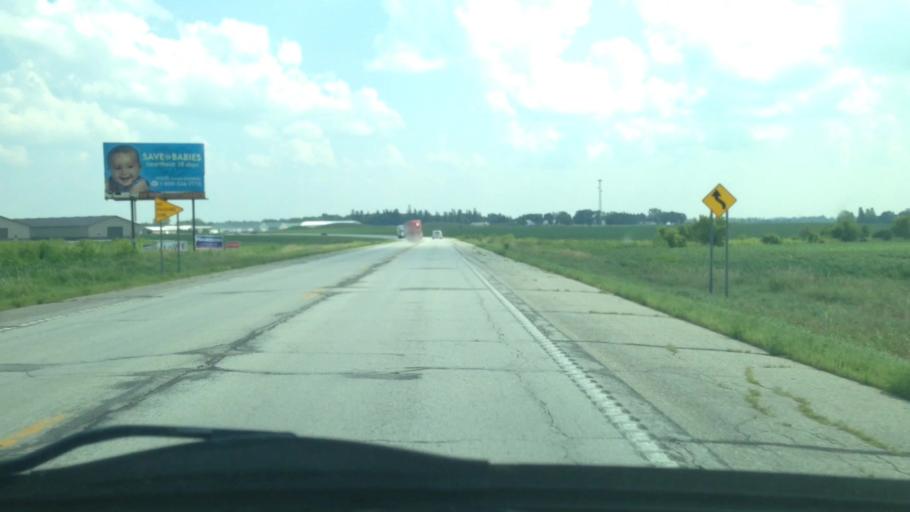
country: US
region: Minnesota
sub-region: Fillmore County
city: Spring Valley
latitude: 43.7058
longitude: -92.4146
